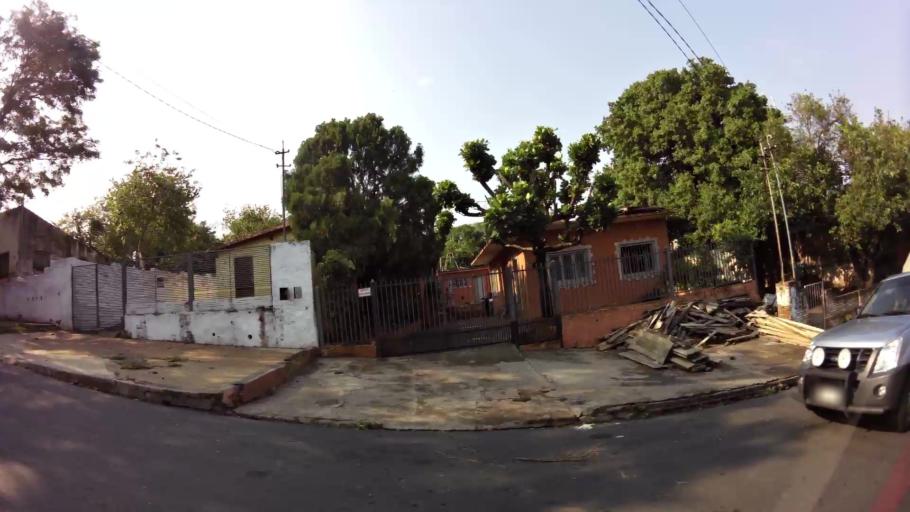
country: PY
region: Presidente Hayes
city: Nanawa
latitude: -25.2819
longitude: -57.6645
